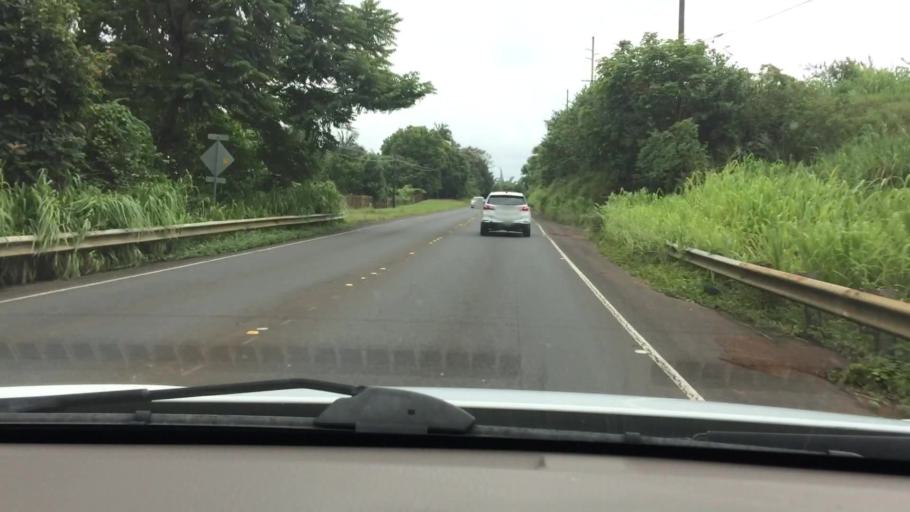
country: US
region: Hawaii
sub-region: Hawaii County
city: Papa'ikou
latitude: 19.7676
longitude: -155.0917
